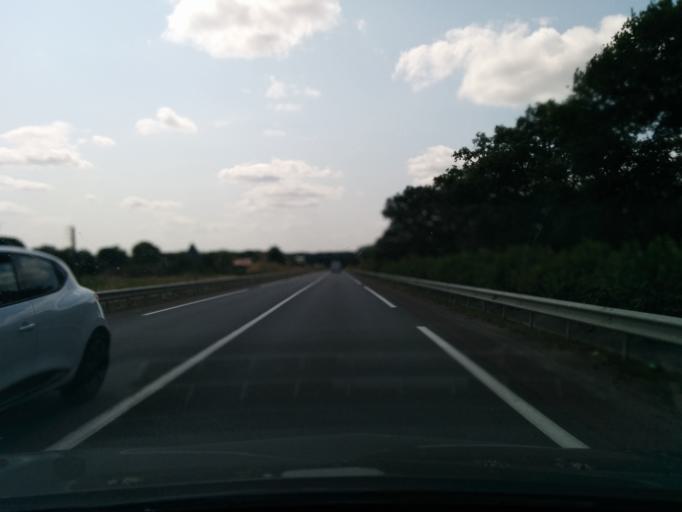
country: FR
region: Centre
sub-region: Departement du Cher
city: Vierzon
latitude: 47.2457
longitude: 2.0739
